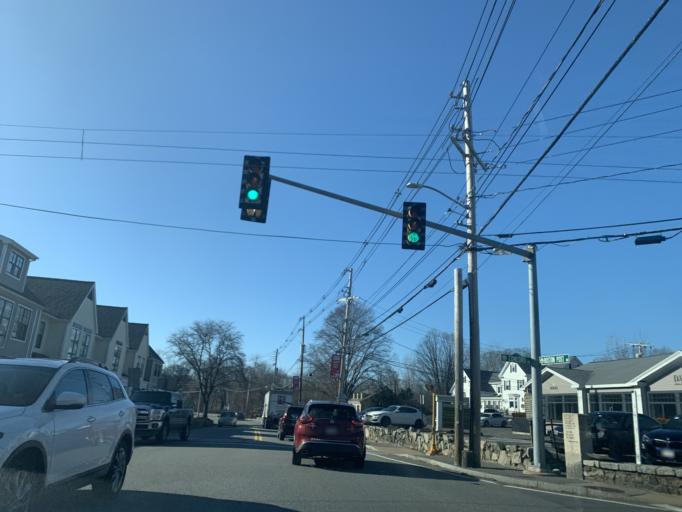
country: US
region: Massachusetts
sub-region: Middlesex County
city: Sudbury
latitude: 42.3622
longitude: -71.4160
